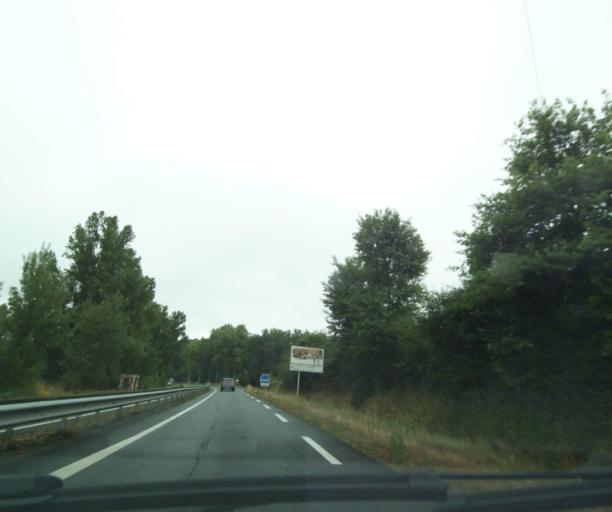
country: FR
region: Midi-Pyrenees
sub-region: Departement du Tarn
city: Le Garric
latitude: 43.9902
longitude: 2.1746
